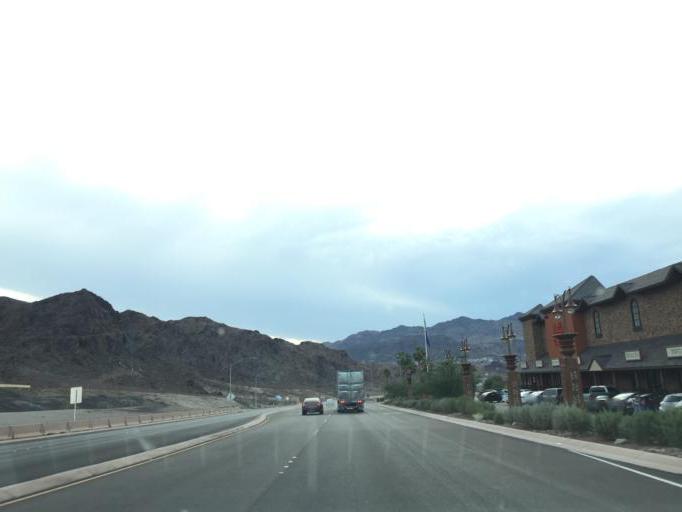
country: US
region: Nevada
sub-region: Clark County
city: Boulder City
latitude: 36.0095
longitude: -114.7842
